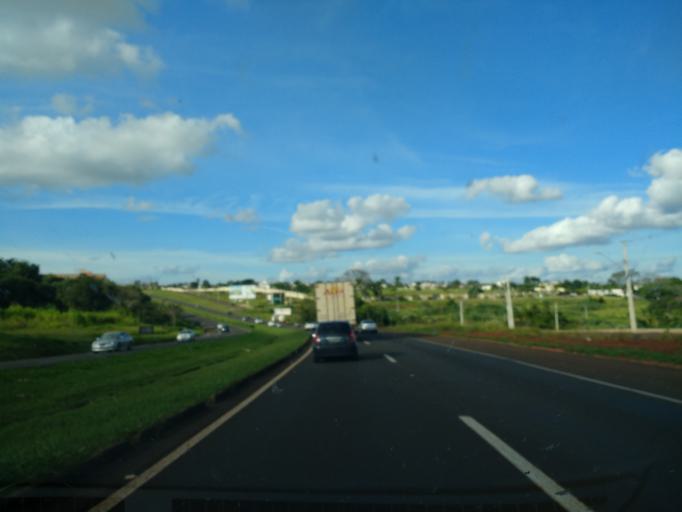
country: BR
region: Parana
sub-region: Cambe
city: Cambe
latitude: -23.2964
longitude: -51.2733
